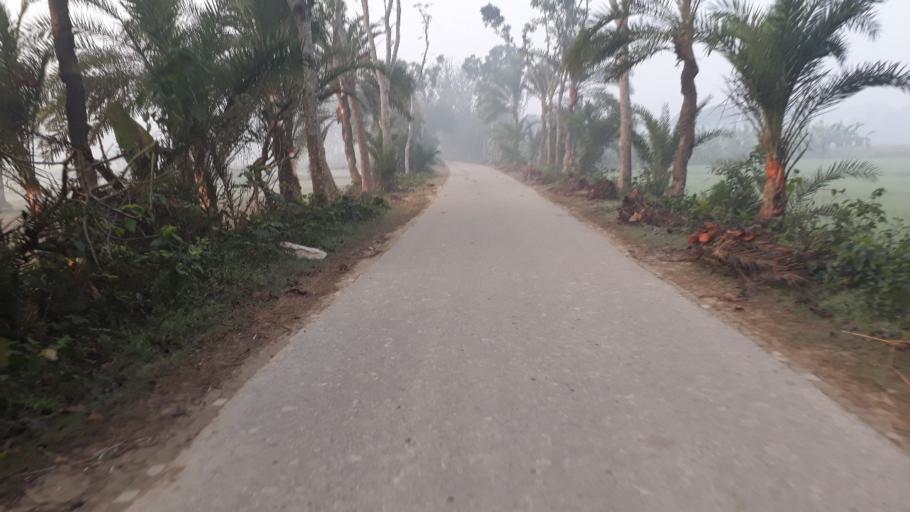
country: BD
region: Khulna
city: Jhingergacha
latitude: 23.2621
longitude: 88.9332
